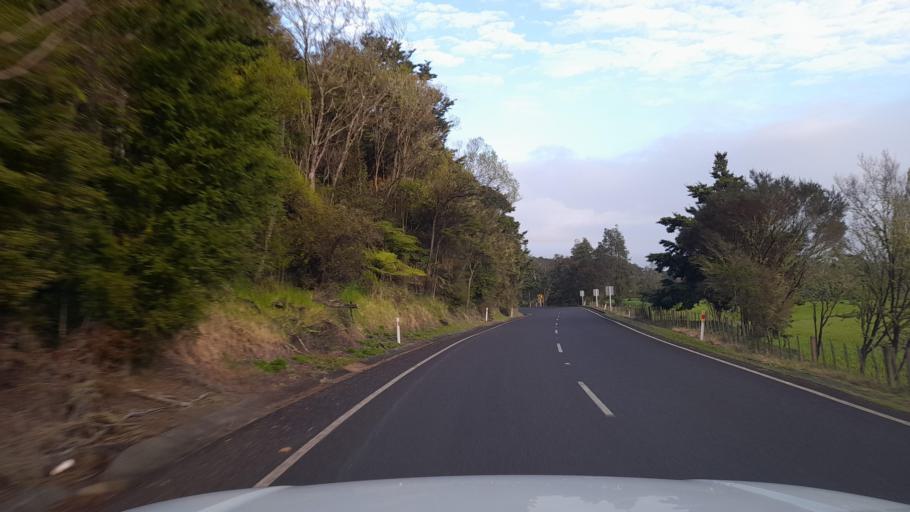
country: NZ
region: Northland
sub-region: Kaipara District
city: Dargaville
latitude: -35.6584
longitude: 173.8793
